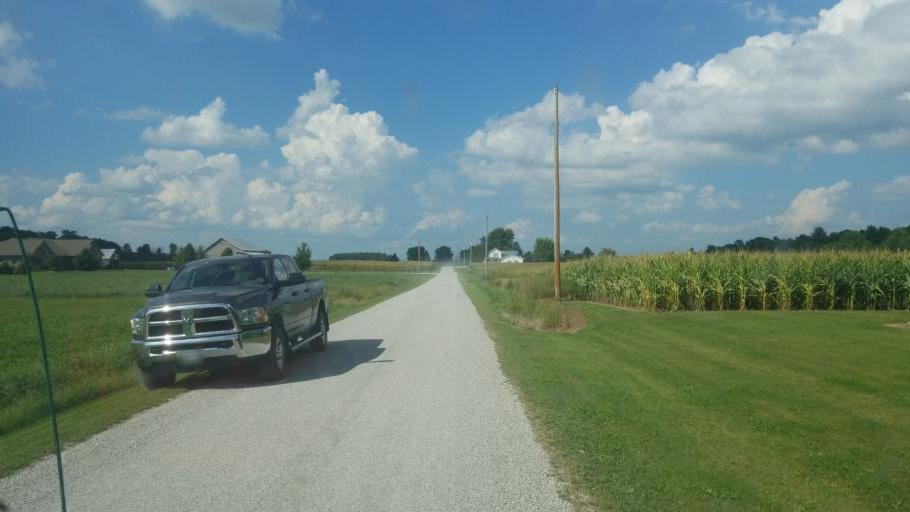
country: US
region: Ohio
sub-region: Huron County
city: Willard
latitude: 40.9872
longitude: -82.7966
